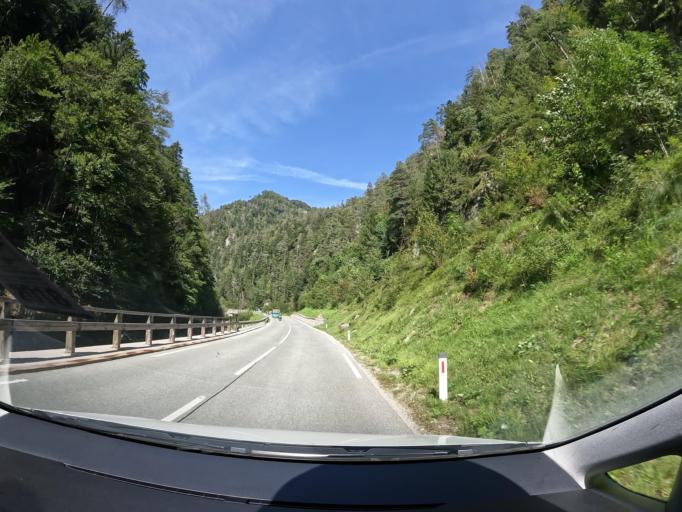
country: SI
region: Trzic
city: Trzic
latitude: 46.4248
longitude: 14.2797
